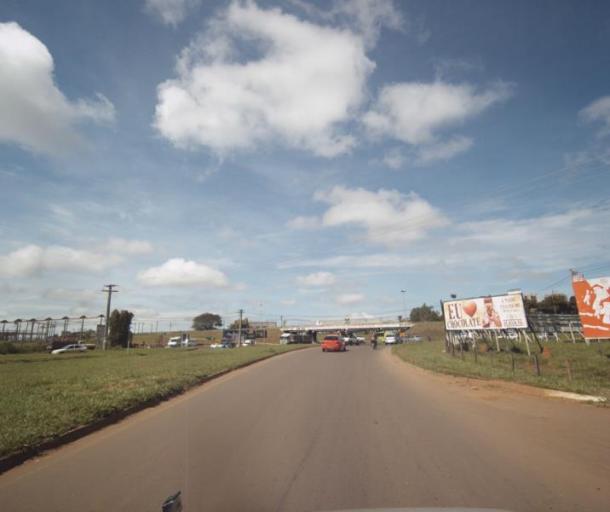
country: BR
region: Goias
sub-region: Anapolis
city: Anapolis
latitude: -16.2853
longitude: -48.9437
